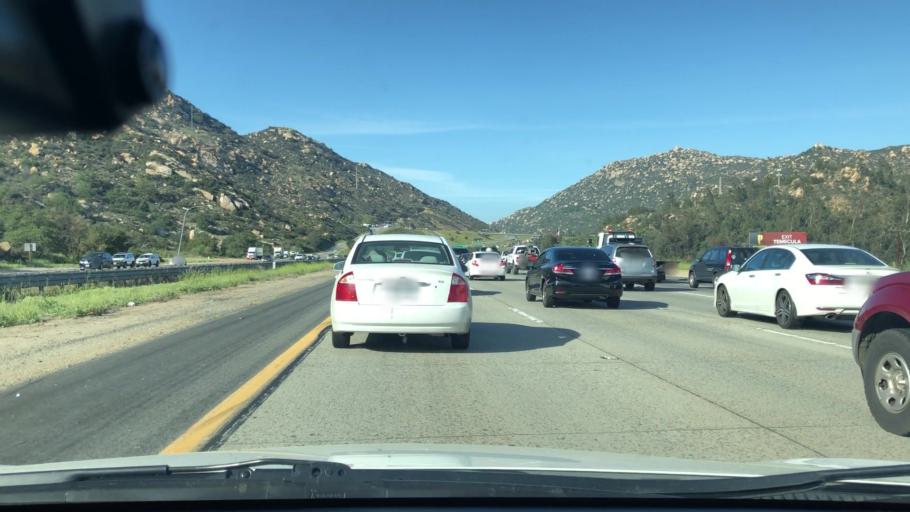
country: US
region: California
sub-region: San Diego County
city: Rainbow
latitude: 33.4219
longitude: -117.1535
